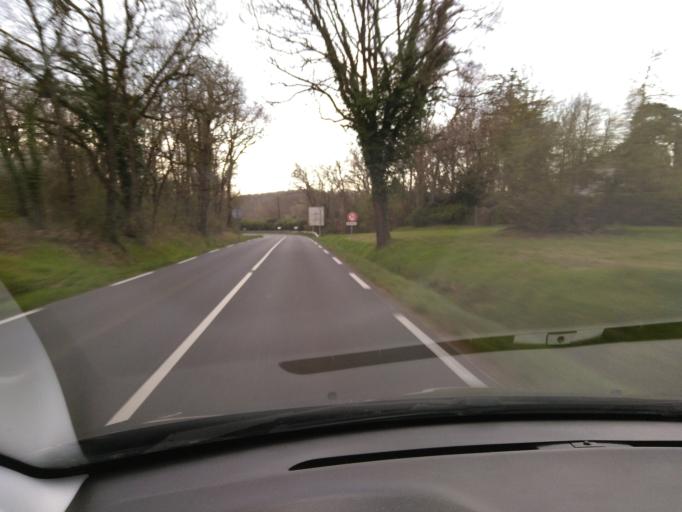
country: FR
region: Midi-Pyrenees
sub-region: Departement de la Haute-Garonne
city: Brax
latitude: 43.6144
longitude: 1.2604
